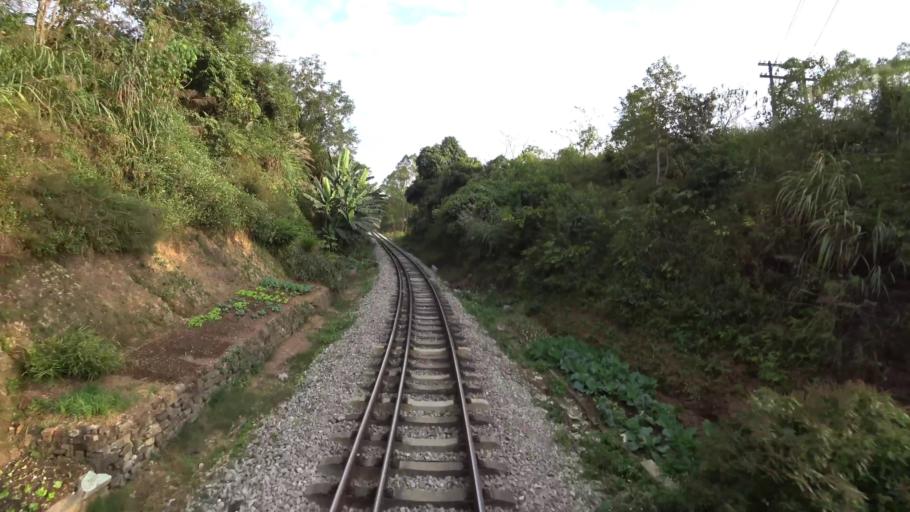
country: VN
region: Lang Son
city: Thi Tran Cao Loc
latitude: 21.9347
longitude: 106.6975
